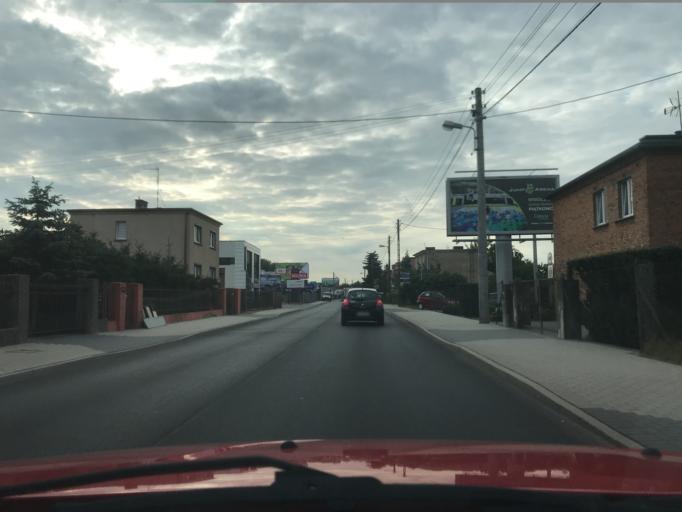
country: PL
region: Greater Poland Voivodeship
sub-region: Powiat poznanski
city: Plewiska
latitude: 52.3881
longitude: 16.8151
